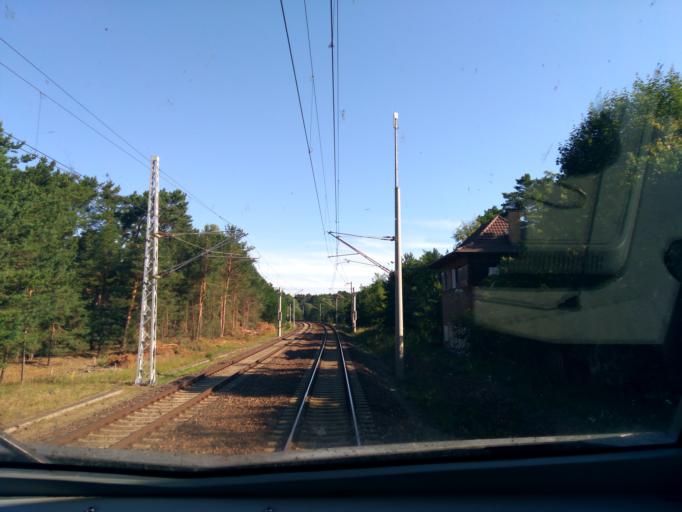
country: DE
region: Brandenburg
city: Gross Koris
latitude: 52.1652
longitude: 13.6487
